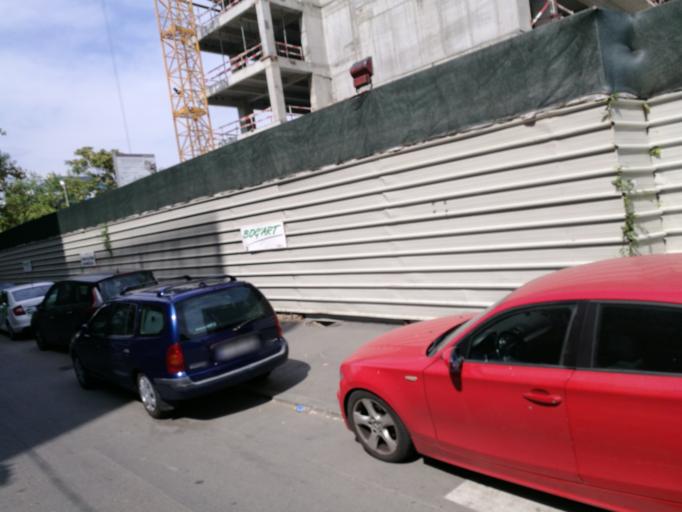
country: RO
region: Bucuresti
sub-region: Municipiul Bucuresti
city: Bucharest
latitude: 44.4796
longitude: 26.1160
